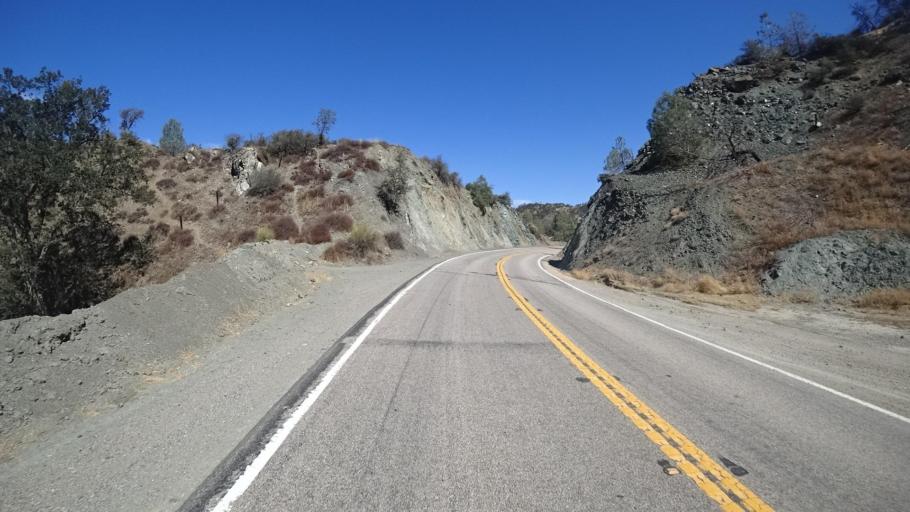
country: US
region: California
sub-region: Fresno County
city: Coalinga
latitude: 36.2024
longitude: -120.7364
